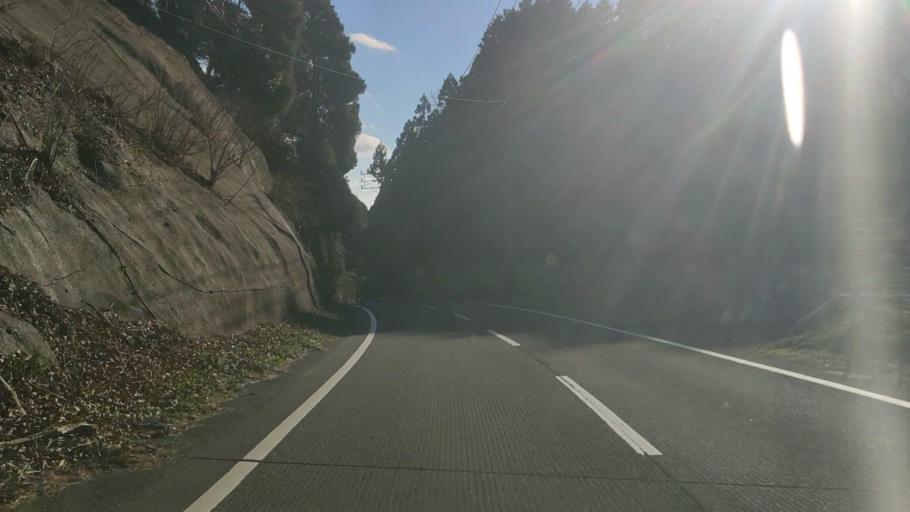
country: JP
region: Saga Prefecture
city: Kanzakimachi-kanzaki
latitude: 33.3964
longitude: 130.2715
